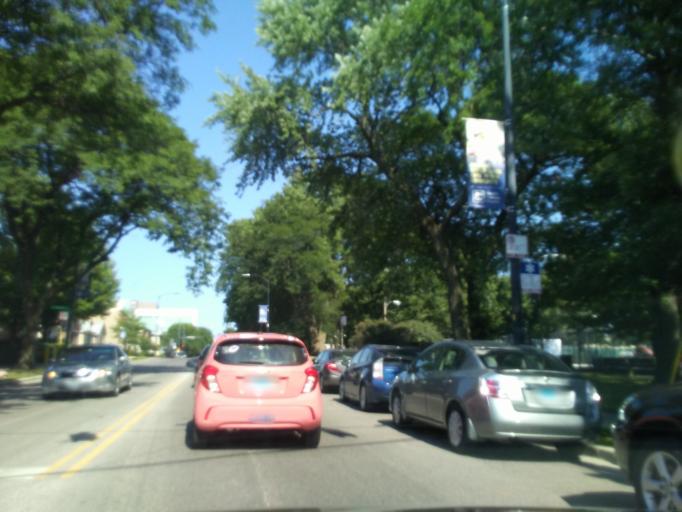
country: US
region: Illinois
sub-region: Cook County
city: Lincolnwood
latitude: 41.9758
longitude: -87.7035
